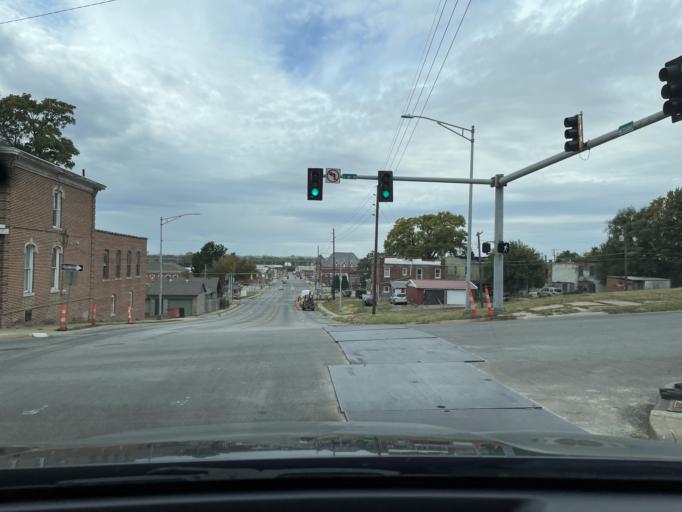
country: US
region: Missouri
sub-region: Buchanan County
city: Saint Joseph
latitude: 39.7625
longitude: -94.8479
